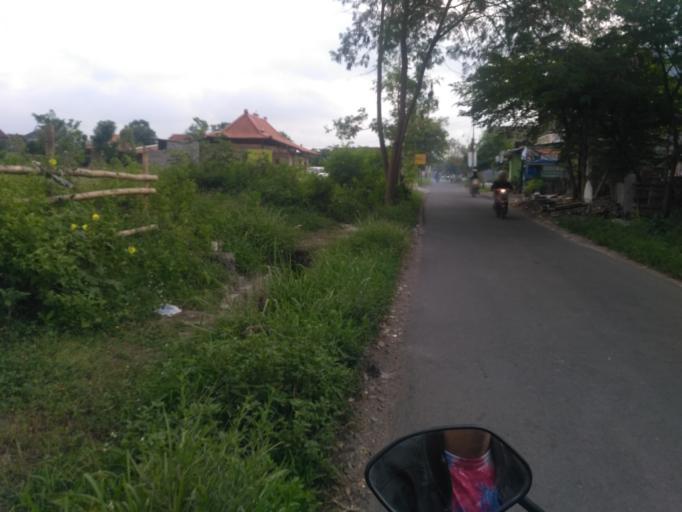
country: ID
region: Daerah Istimewa Yogyakarta
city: Yogyakarta
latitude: -7.7684
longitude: 110.3589
